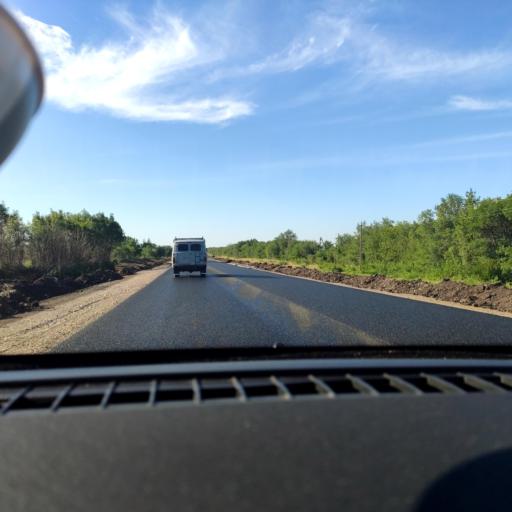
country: RU
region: Samara
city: Krasnoarmeyskoye
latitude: 52.8140
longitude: 50.0110
